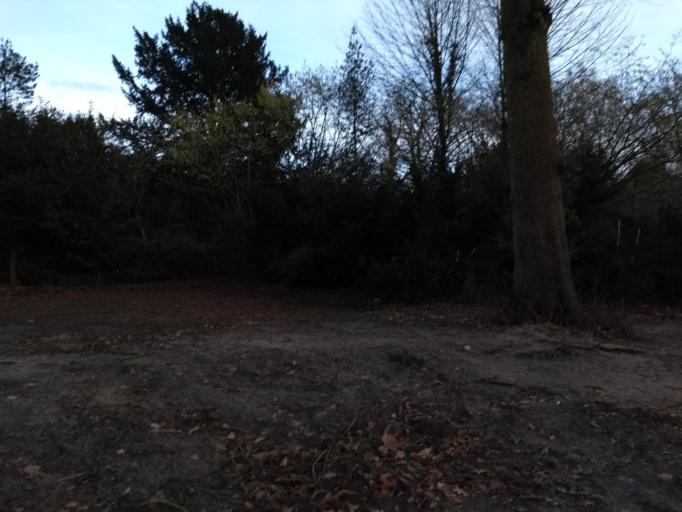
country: NL
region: Overijssel
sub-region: Gemeente Enschede
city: Enschede
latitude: 52.2506
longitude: 6.8871
